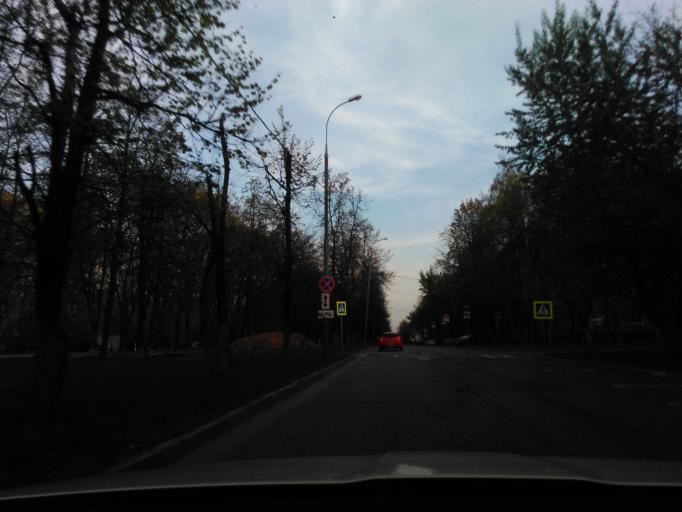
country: RU
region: Moscow
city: Tekstil'shchiki
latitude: 55.7067
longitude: 37.7460
